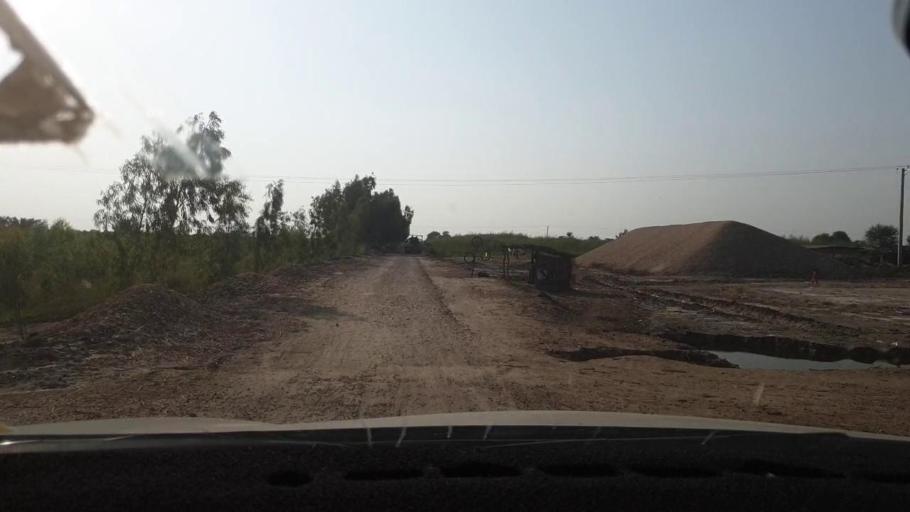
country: PK
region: Sindh
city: Berani
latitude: 25.7521
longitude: 68.7727
